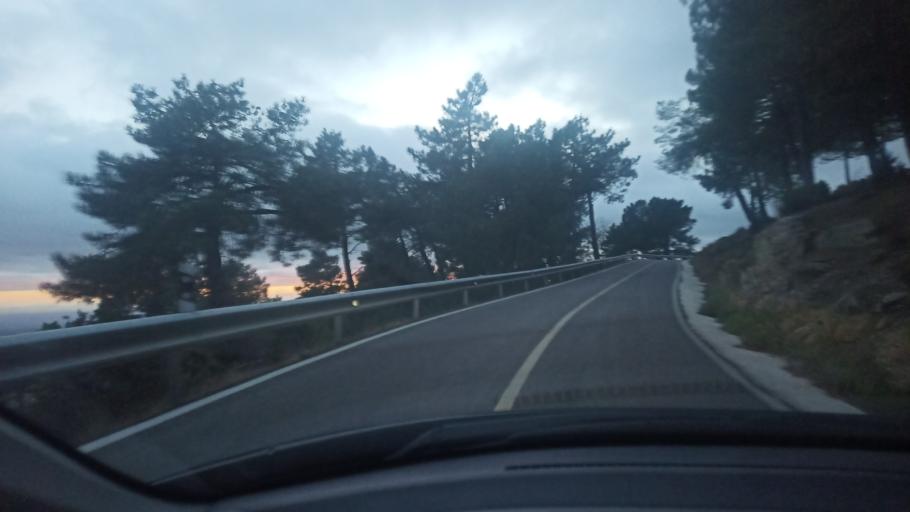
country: ES
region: Madrid
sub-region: Provincia de Madrid
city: Zarzalejo
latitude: 40.5520
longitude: -4.1934
